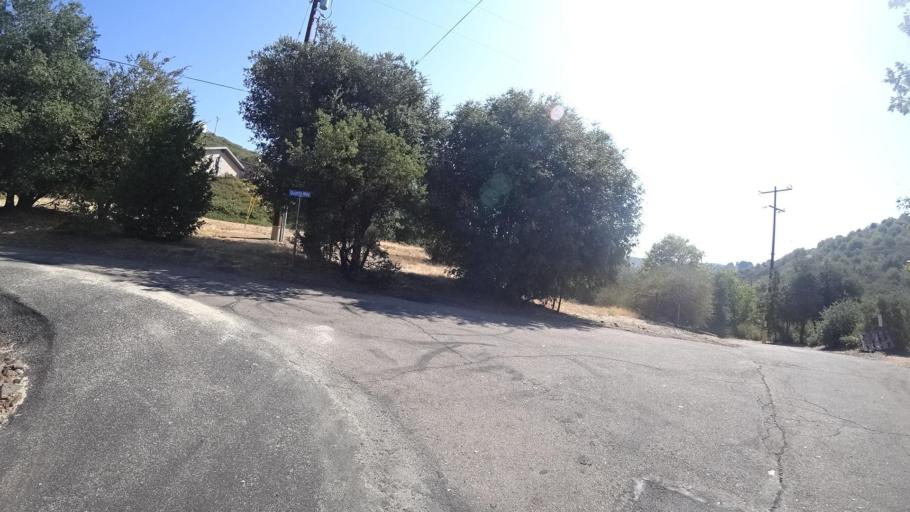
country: US
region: California
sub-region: San Diego County
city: Julian
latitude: 33.0260
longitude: -116.5690
